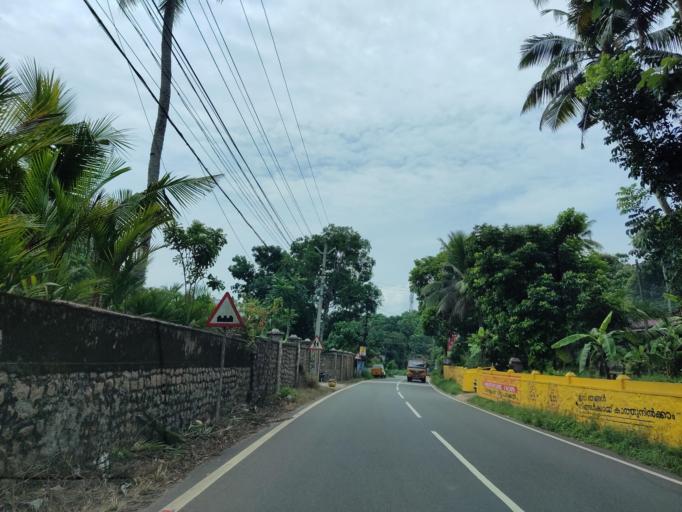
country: IN
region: Kerala
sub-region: Alappuzha
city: Chengannur
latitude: 9.2981
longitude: 76.6266
